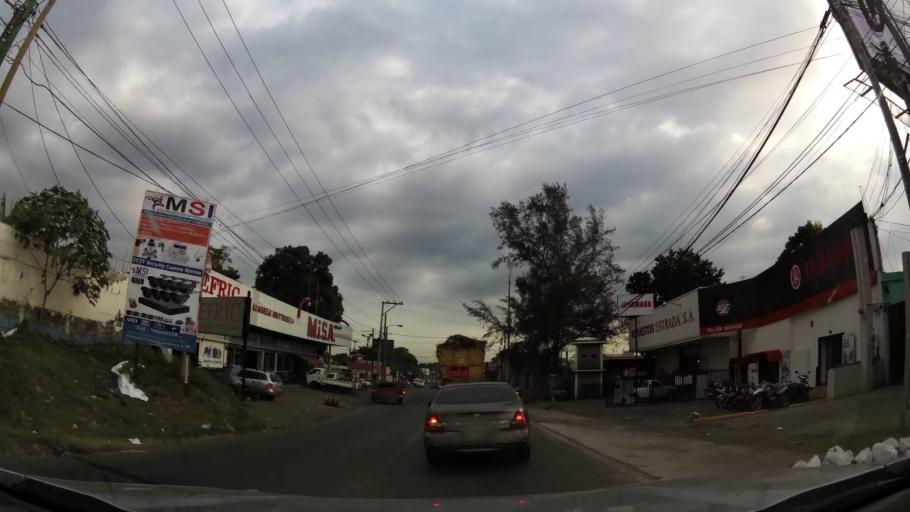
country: GT
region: Escuintla
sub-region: Municipio de Escuintla
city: Escuintla
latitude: 14.3045
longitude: -90.7816
